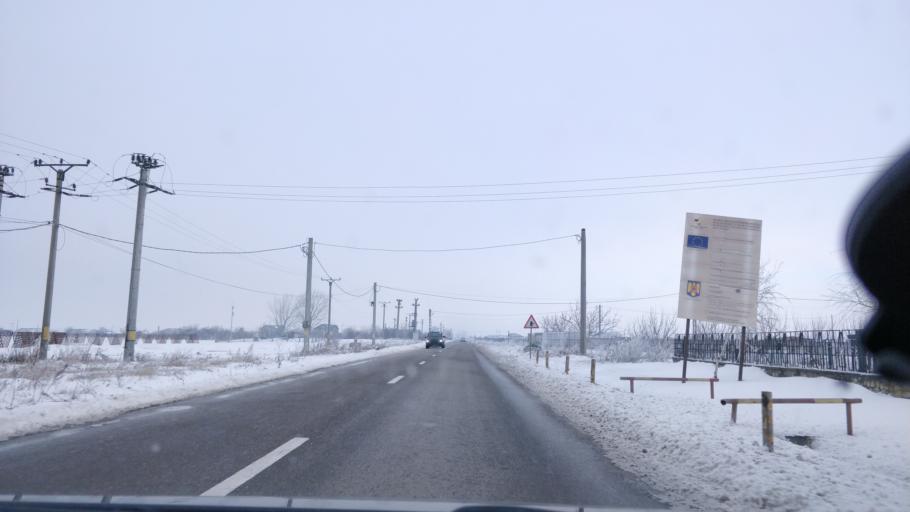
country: RO
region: Vrancea
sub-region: Comuna Vrancioaia
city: Focsani
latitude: 45.6979
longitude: 27.2129
